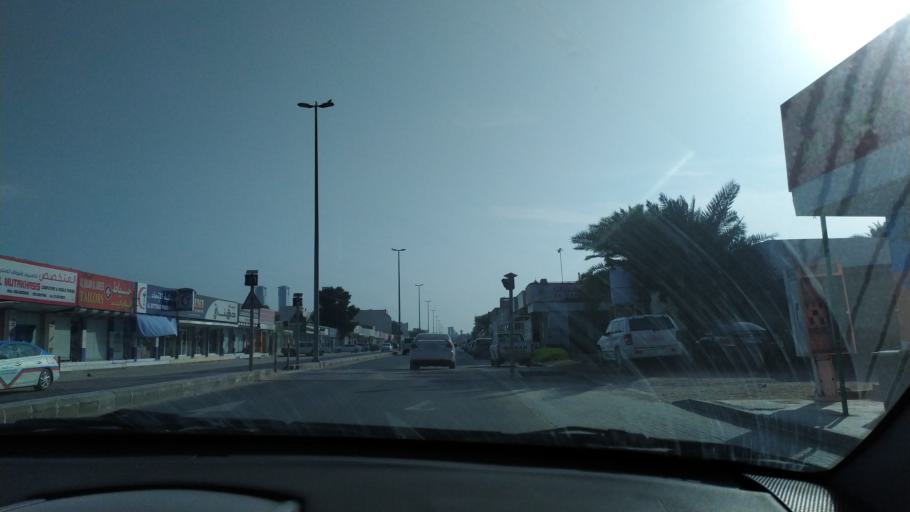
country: AE
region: Ra's al Khaymah
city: Ras al-Khaimah
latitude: 25.8102
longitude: 55.9642
